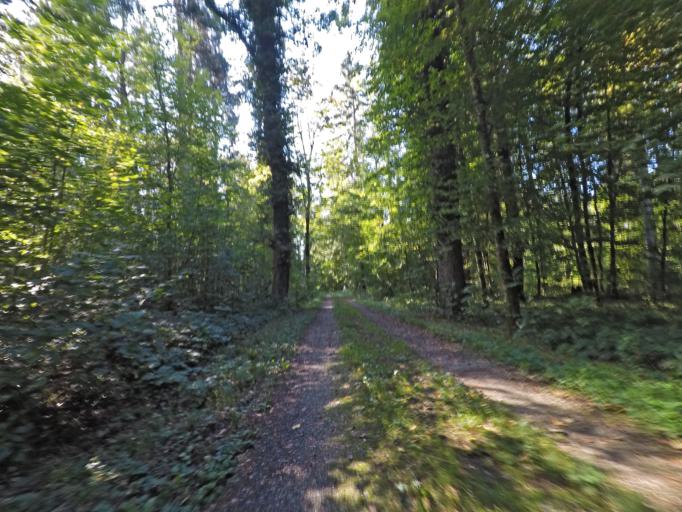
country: CH
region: Thurgau
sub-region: Frauenfeld District
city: Diessenhofen
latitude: 47.6560
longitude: 8.7453
